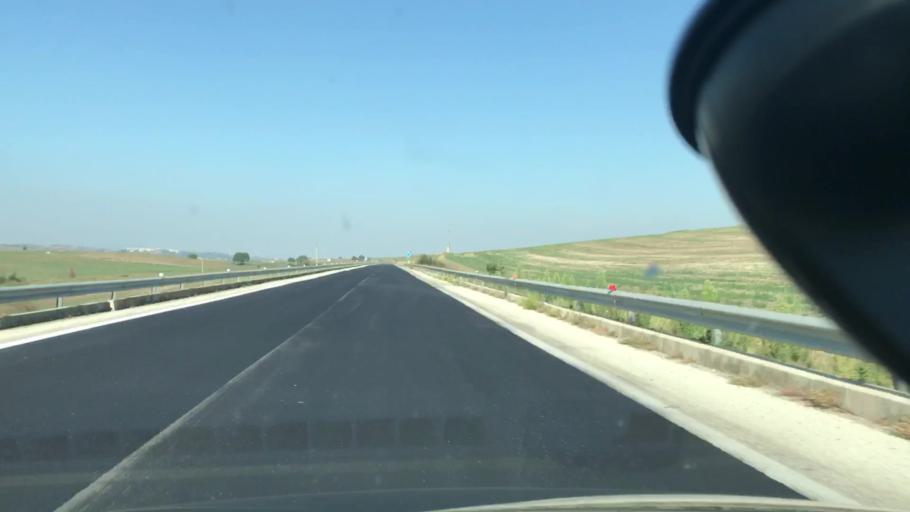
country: IT
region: Apulia
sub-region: Provincia di Barletta - Andria - Trani
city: Spinazzola
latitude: 40.9222
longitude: 16.0920
